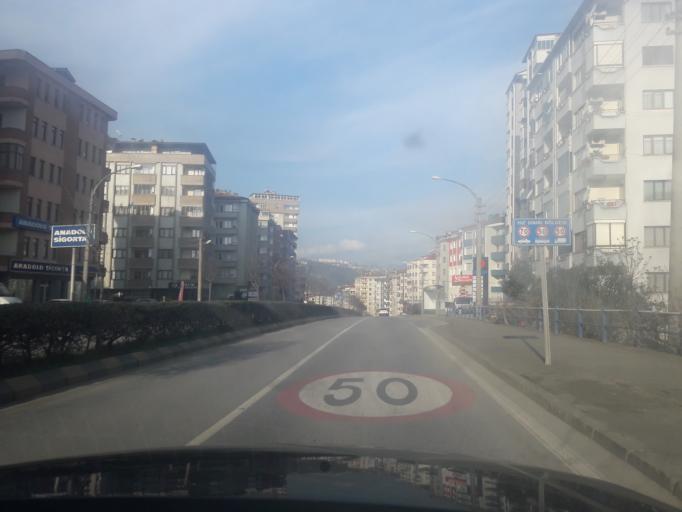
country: TR
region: Trabzon
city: Trabzon
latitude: 40.9964
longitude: 39.6829
